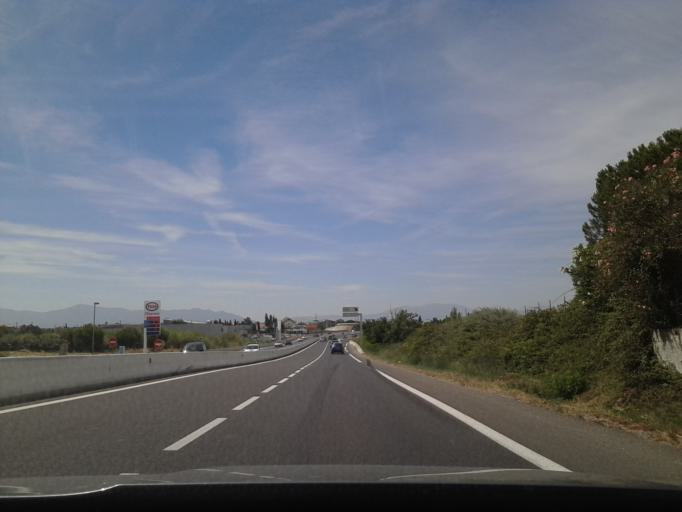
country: FR
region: Languedoc-Roussillon
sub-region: Departement des Pyrenees-Orientales
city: Pia
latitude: 42.7493
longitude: 2.8945
